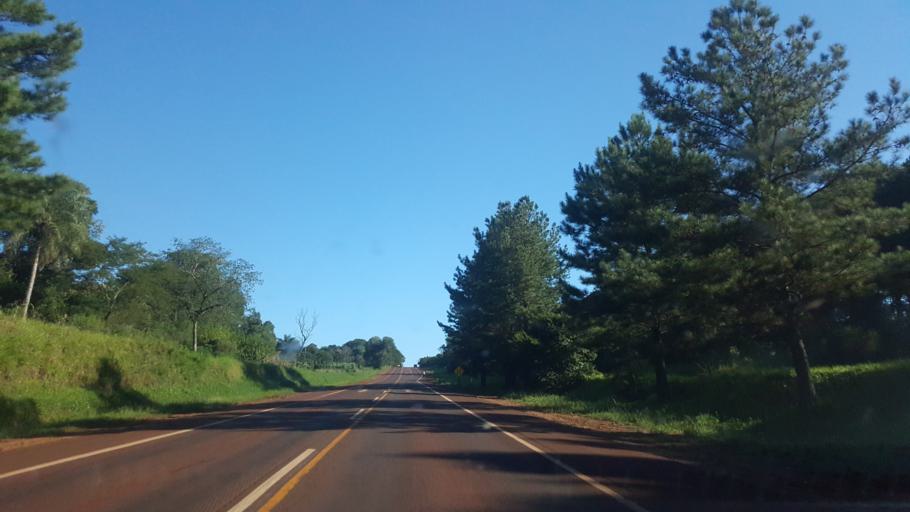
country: AR
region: Misiones
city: Puerto Esperanza
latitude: -26.1549
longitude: -54.5831
